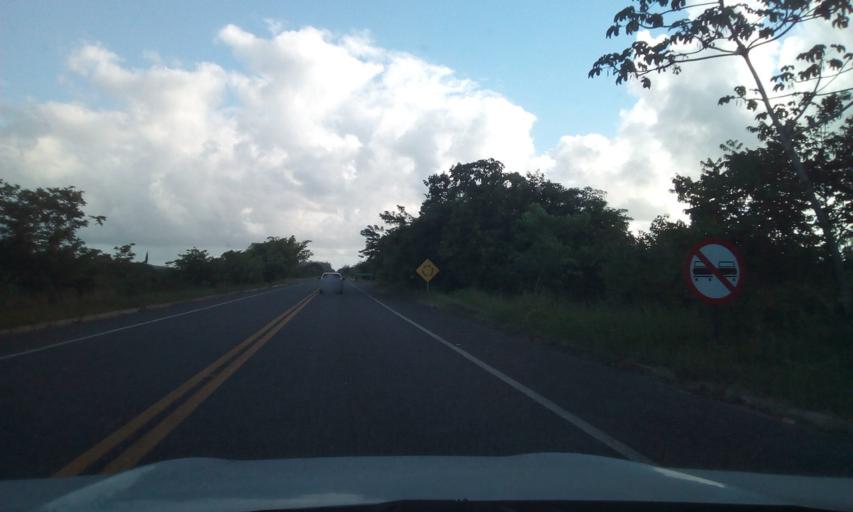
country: BR
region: Bahia
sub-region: Entre Rios
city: Entre Rios
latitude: -12.2999
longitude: -37.8988
